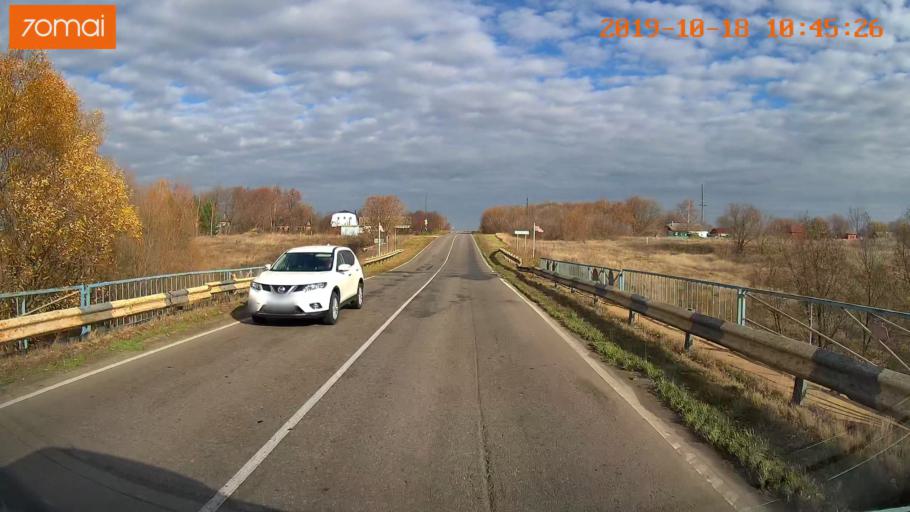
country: RU
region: Tula
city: Yepifan'
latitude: 53.6707
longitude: 38.6901
